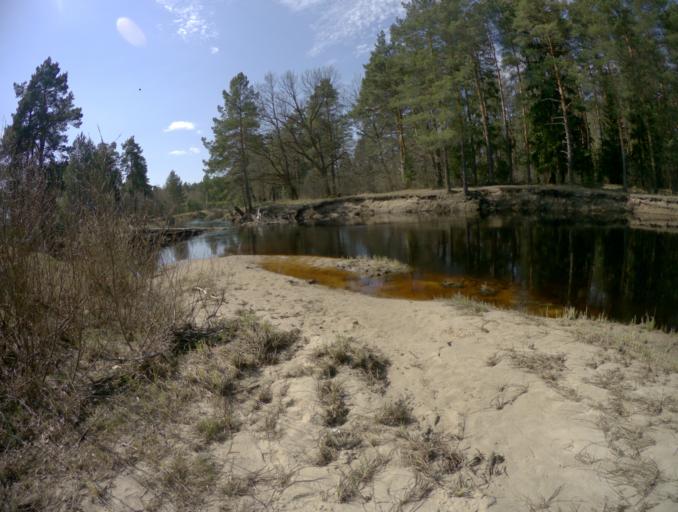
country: RU
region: Vladimir
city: Mezinovskiy
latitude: 55.5434
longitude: 40.2632
